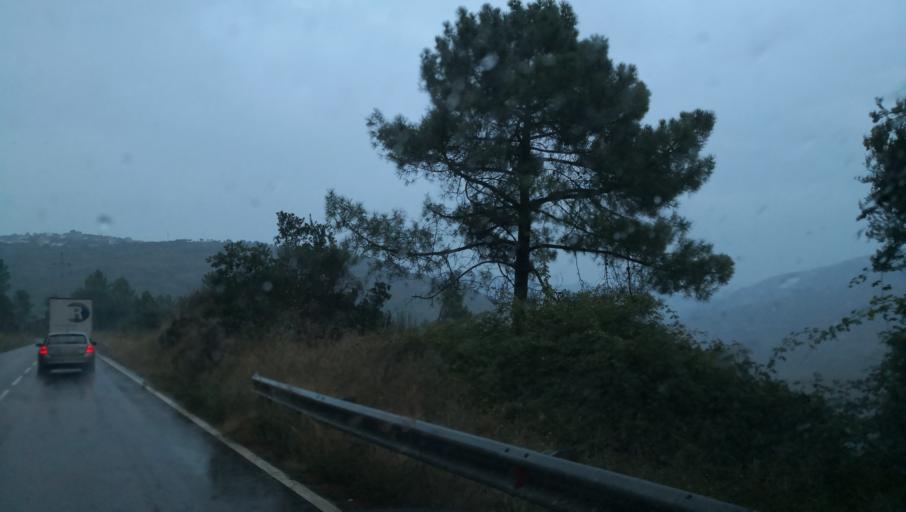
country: PT
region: Vila Real
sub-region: Santa Marta de Penaguiao
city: Santa Marta de Penaguiao
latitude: 41.2163
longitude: -7.7285
